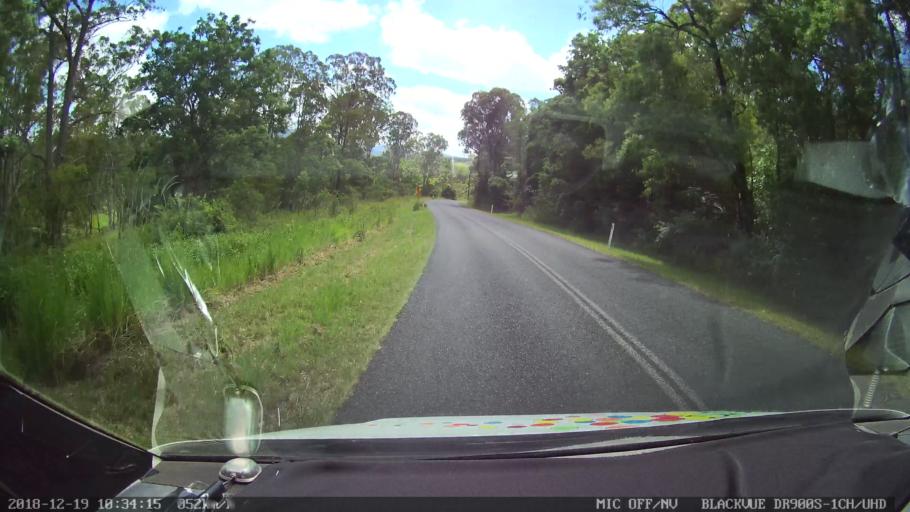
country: AU
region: New South Wales
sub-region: Lismore Municipality
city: Larnook
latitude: -28.5788
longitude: 153.1296
